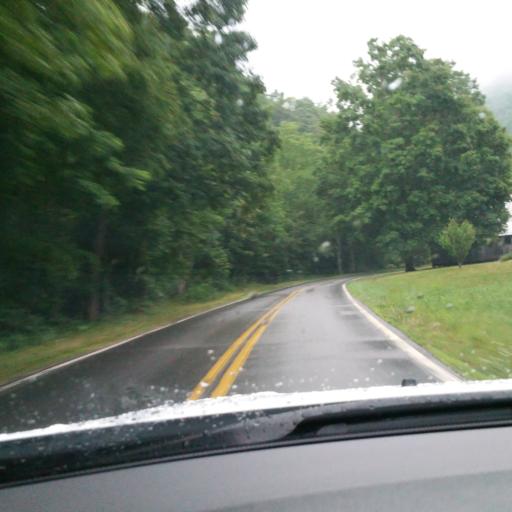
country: US
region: North Carolina
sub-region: Yancey County
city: Burnsville
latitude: 35.8851
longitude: -82.2845
